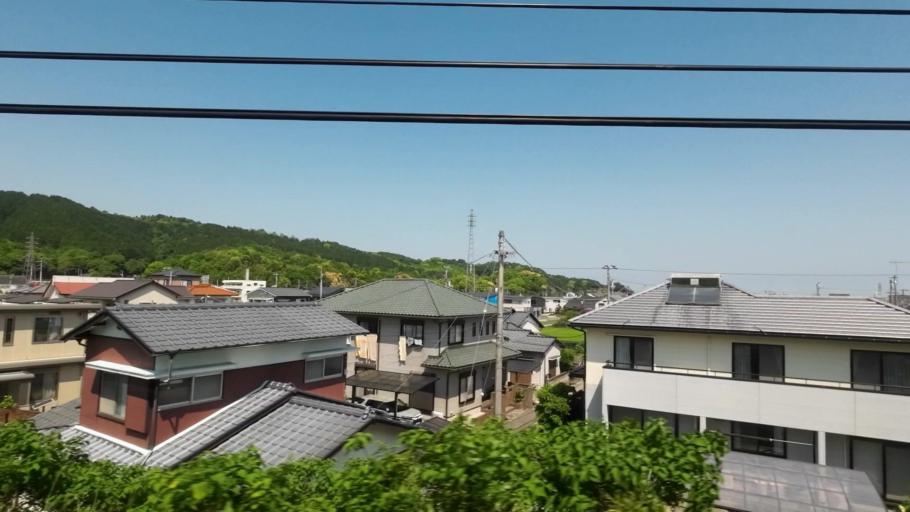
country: JP
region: Ehime
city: Niihama
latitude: 33.9401
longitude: 133.2858
